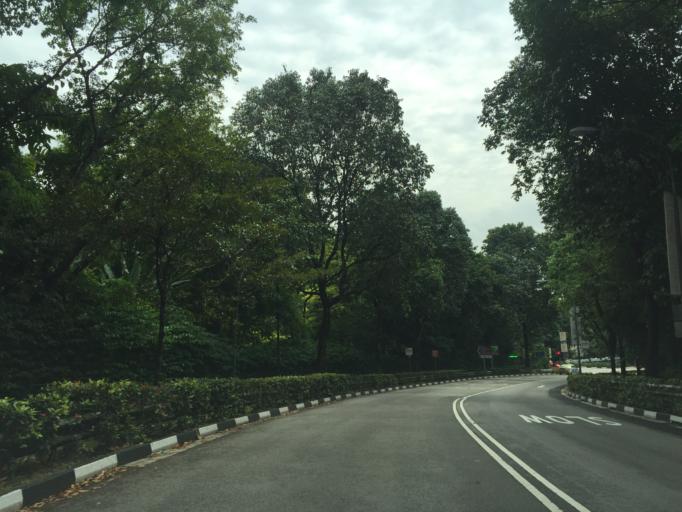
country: SG
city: Singapore
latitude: 1.3147
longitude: 103.8172
